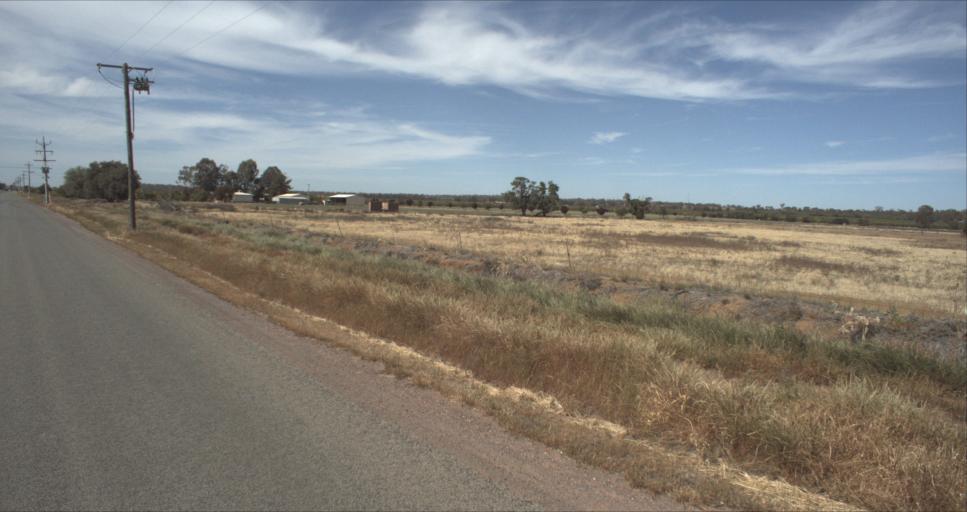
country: AU
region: New South Wales
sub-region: Leeton
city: Leeton
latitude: -34.5790
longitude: 146.4683
